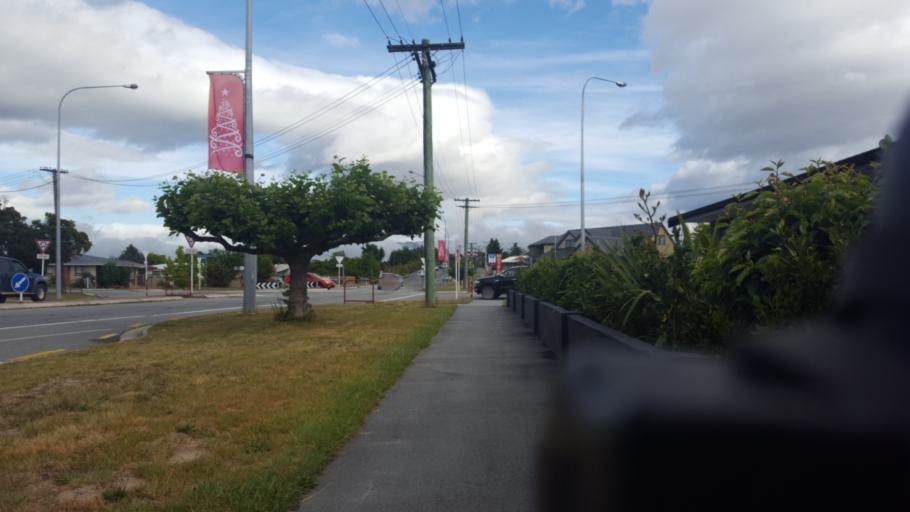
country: NZ
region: Otago
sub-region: Queenstown-Lakes District
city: Wanaka
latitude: -45.2481
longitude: 169.3849
